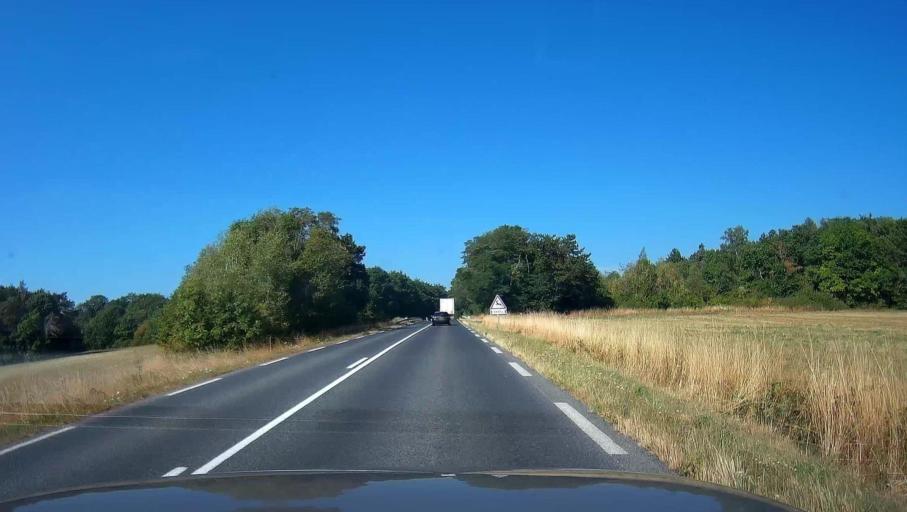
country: FR
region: Lorraine
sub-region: Departement de Meurthe-et-Moselle
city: Chaligny
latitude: 48.5783
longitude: 6.0042
